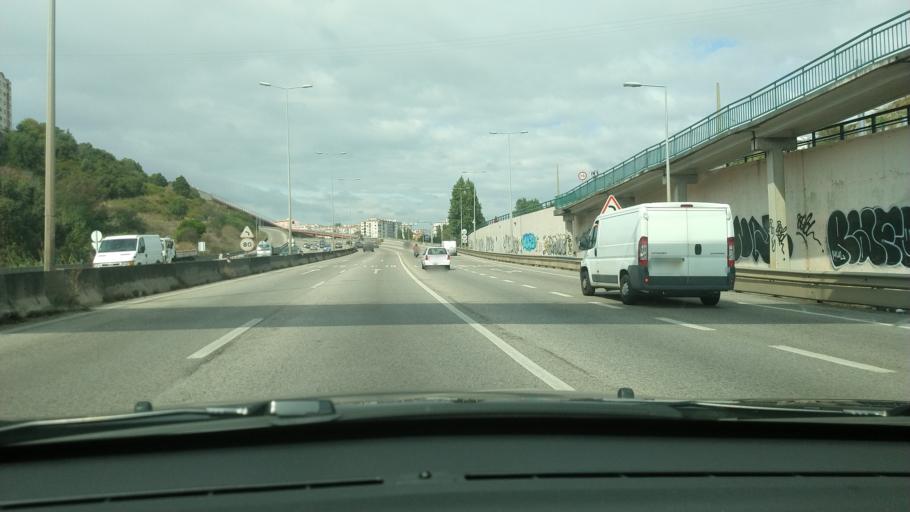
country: PT
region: Lisbon
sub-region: Sintra
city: Cacem
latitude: 38.7629
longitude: -9.2970
